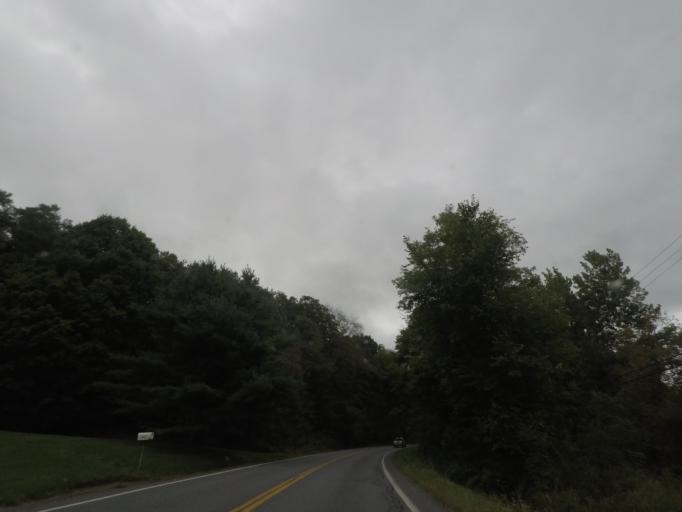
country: US
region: New York
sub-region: Rensselaer County
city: Hoosick Falls
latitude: 42.9519
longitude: -73.3894
